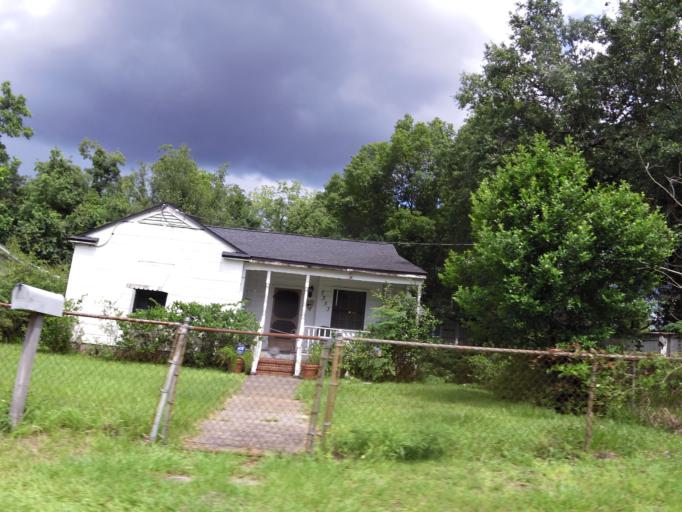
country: US
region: Florida
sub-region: Duval County
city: Jacksonville
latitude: 30.3856
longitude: -81.6408
